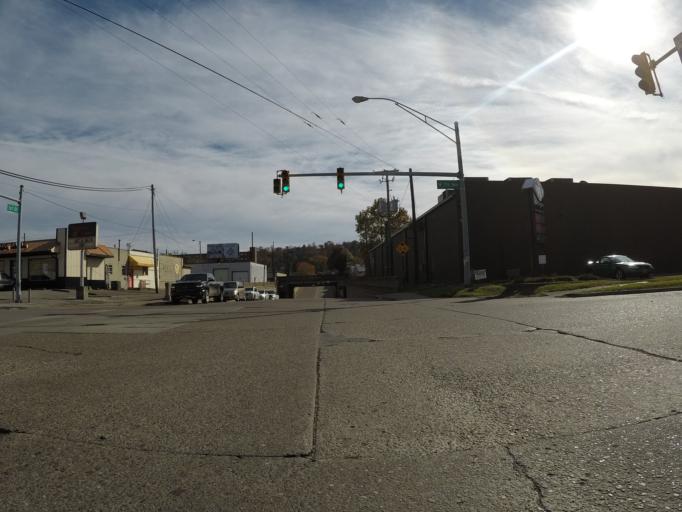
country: US
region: West Virginia
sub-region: Cabell County
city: Huntington
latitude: 38.4144
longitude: -82.4565
